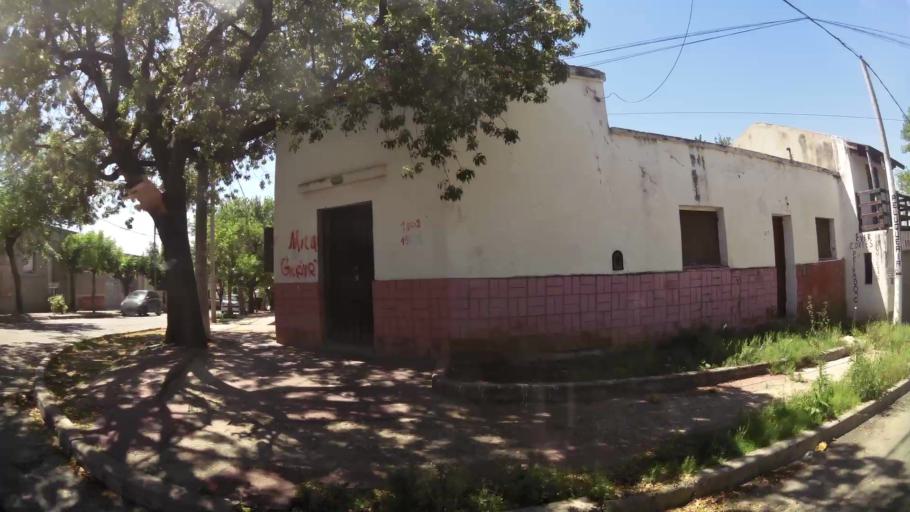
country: AR
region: Cordoba
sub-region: Departamento de Capital
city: Cordoba
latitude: -31.4298
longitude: -64.2029
